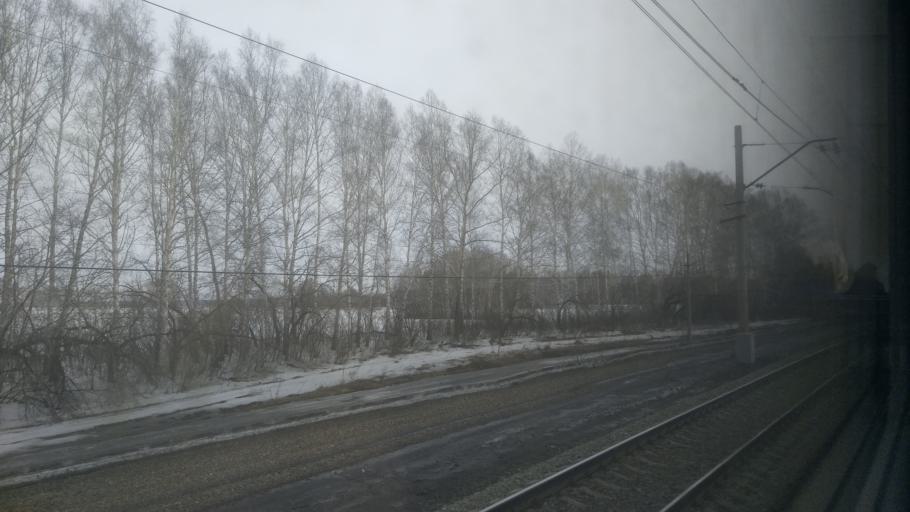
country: RU
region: Novosibirsk
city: Bolotnoye
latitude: 55.7092
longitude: 84.6170
